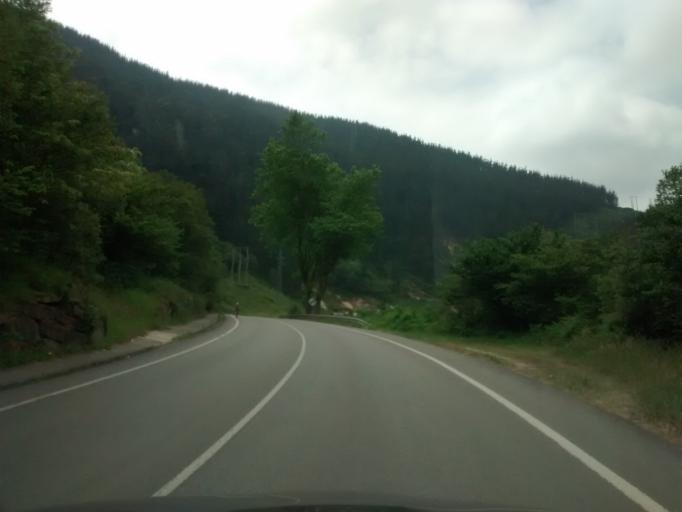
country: ES
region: Cantabria
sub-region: Provincia de Cantabria
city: Cabezon de la Sal
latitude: 43.2794
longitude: -4.2382
